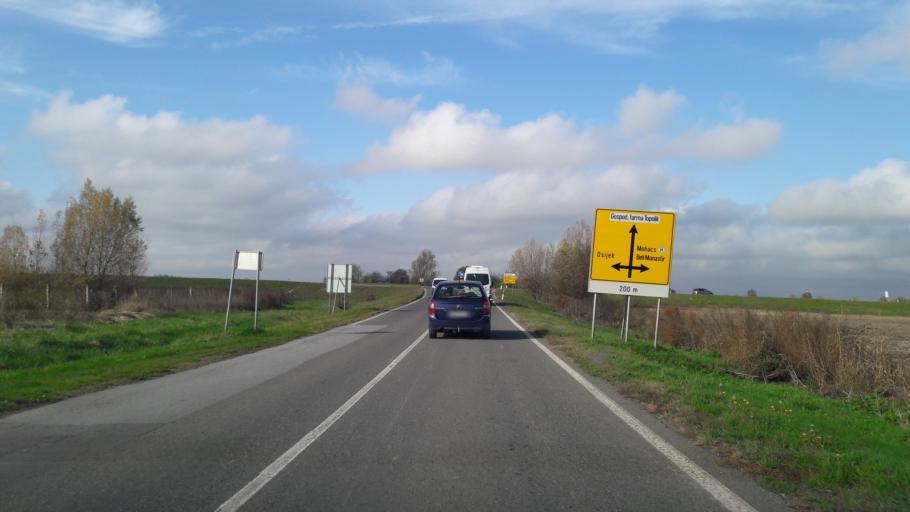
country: HR
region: Osjecko-Baranjska
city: Darda
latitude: 45.6201
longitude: 18.6782
